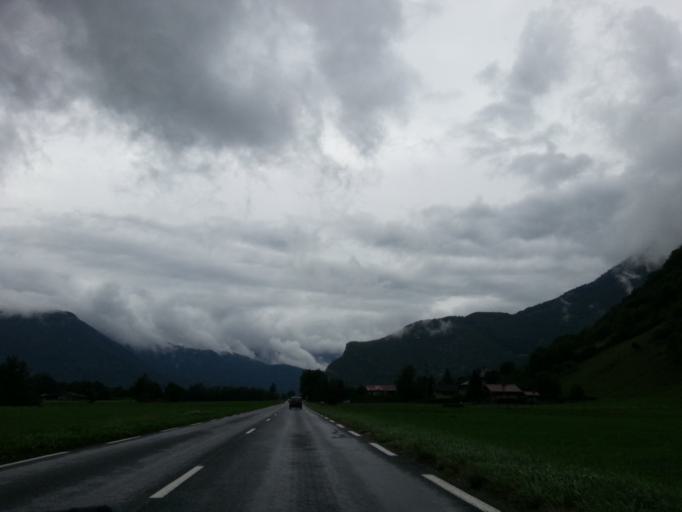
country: FR
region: Rhone-Alpes
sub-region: Departement de la Haute-Savoie
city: Faverges
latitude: 45.7615
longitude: 6.3297
